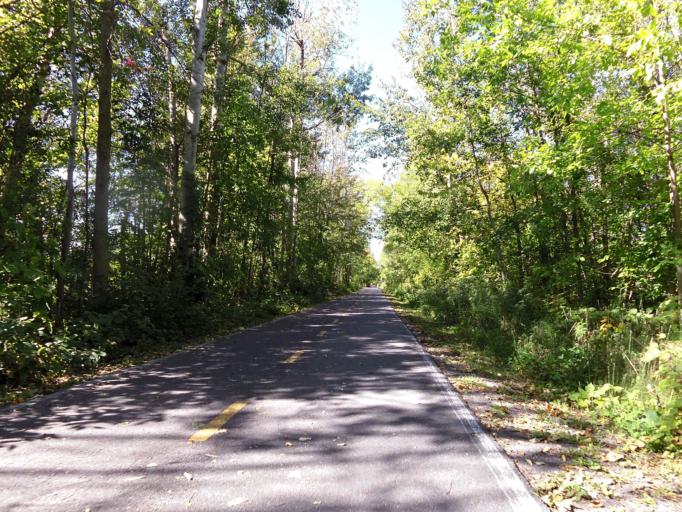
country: CA
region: Ontario
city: Bourget
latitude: 45.2682
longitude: -75.3254
